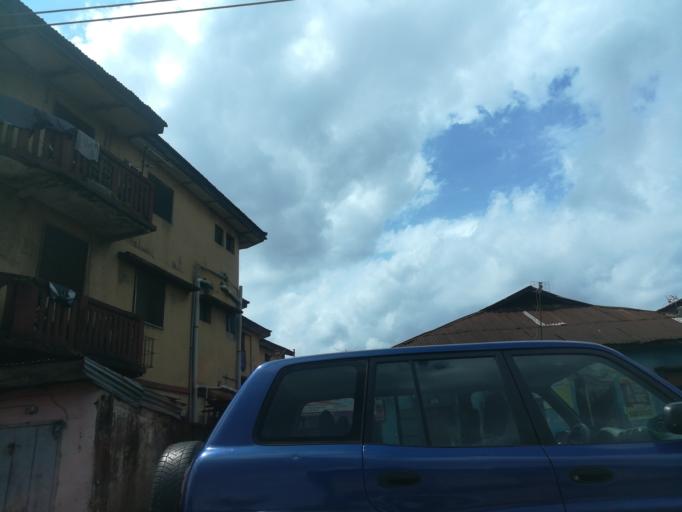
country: NG
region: Lagos
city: Mushin
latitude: 6.5354
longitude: 3.3625
